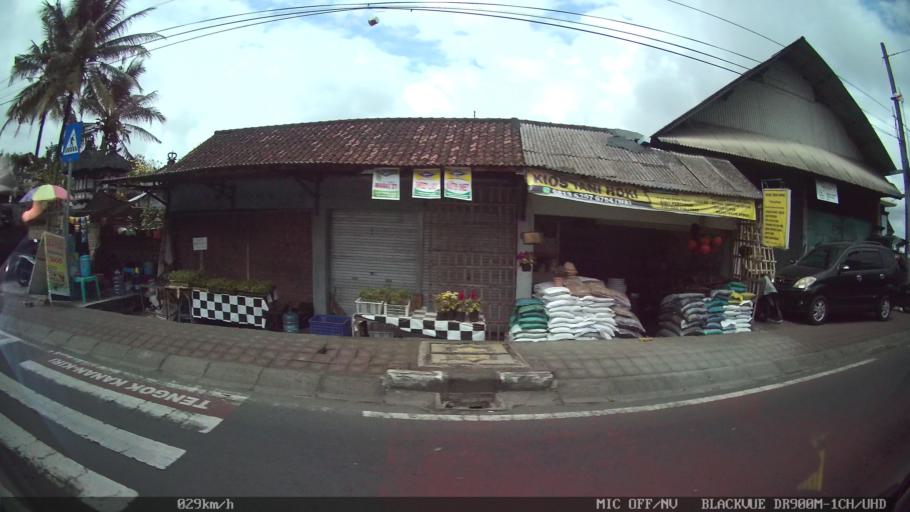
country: ID
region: Bali
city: Banjar Bucu
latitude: -8.5867
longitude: 115.2036
